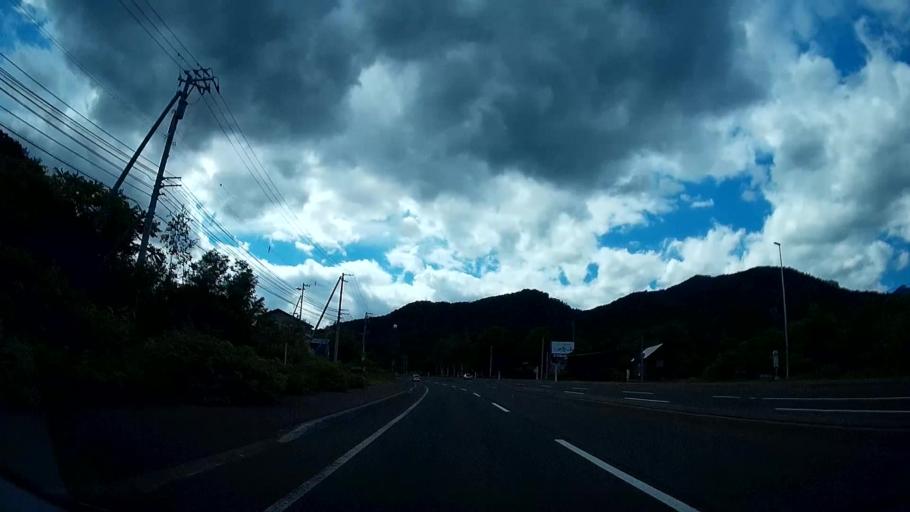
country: JP
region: Hokkaido
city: Sapporo
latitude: 42.9689
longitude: 141.2119
